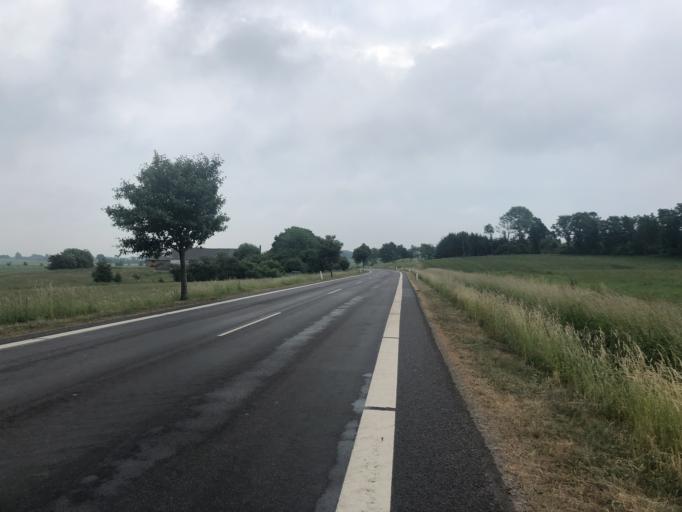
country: DK
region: Capital Region
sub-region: Bornholm Kommune
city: Akirkeby
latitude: 55.1521
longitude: 14.9004
